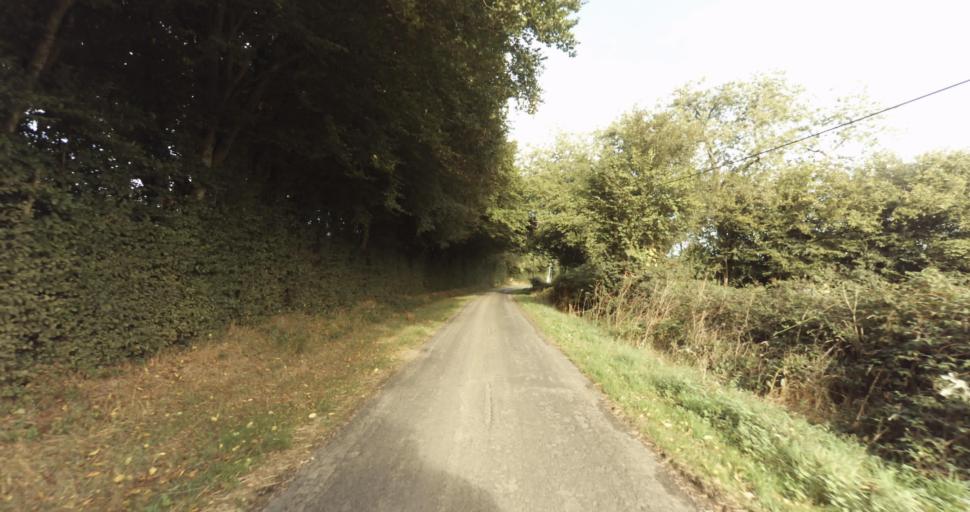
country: FR
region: Lower Normandy
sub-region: Departement de l'Orne
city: Vimoutiers
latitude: 48.8650
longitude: 0.2478
